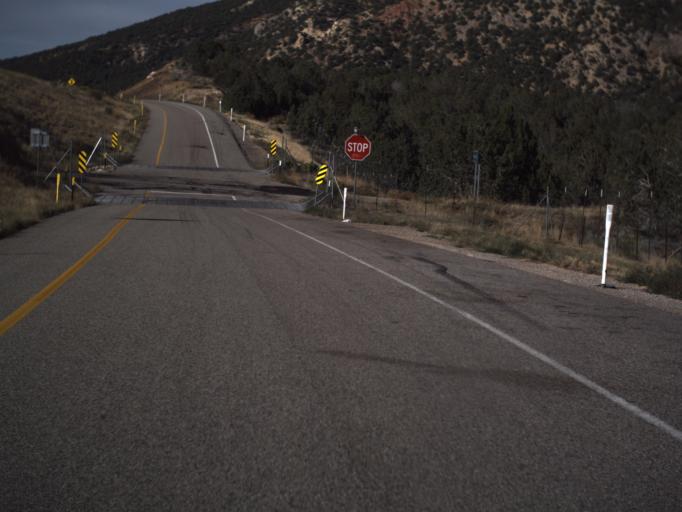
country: US
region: Utah
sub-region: Washington County
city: Toquerville
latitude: 37.4045
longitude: -113.2378
